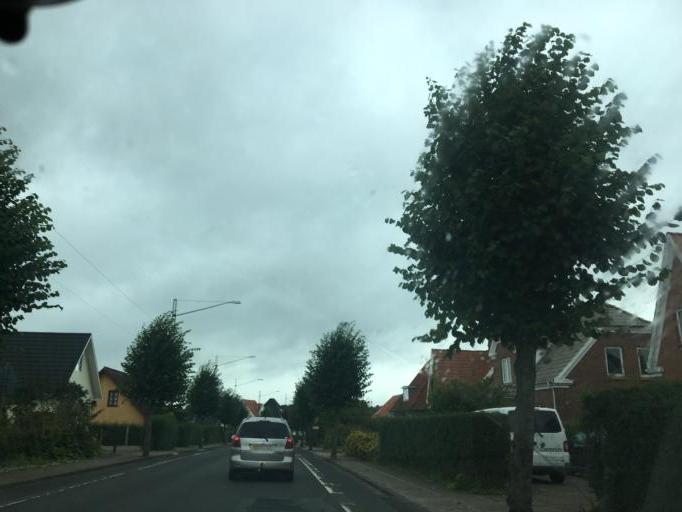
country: DK
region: South Denmark
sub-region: Middelfart Kommune
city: Middelfart
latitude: 55.4962
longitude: 9.7488
